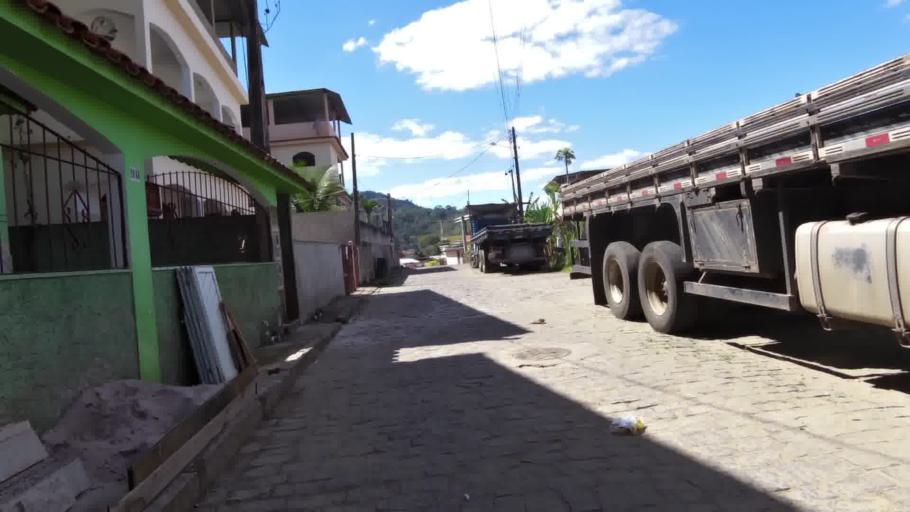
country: BR
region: Espirito Santo
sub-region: Rio Novo Do Sul
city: Rio Novo do Sul
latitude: -20.8668
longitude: -40.9414
